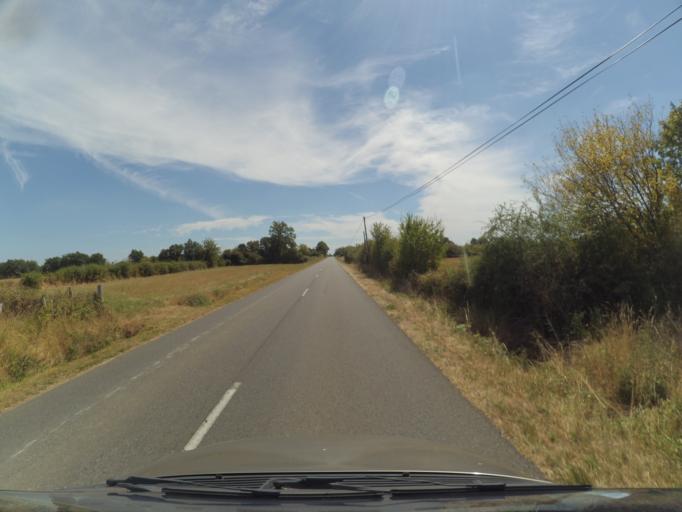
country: FR
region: Poitou-Charentes
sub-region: Departement de la Vienne
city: Availles-Limouzine
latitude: 46.1601
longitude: 0.5503
